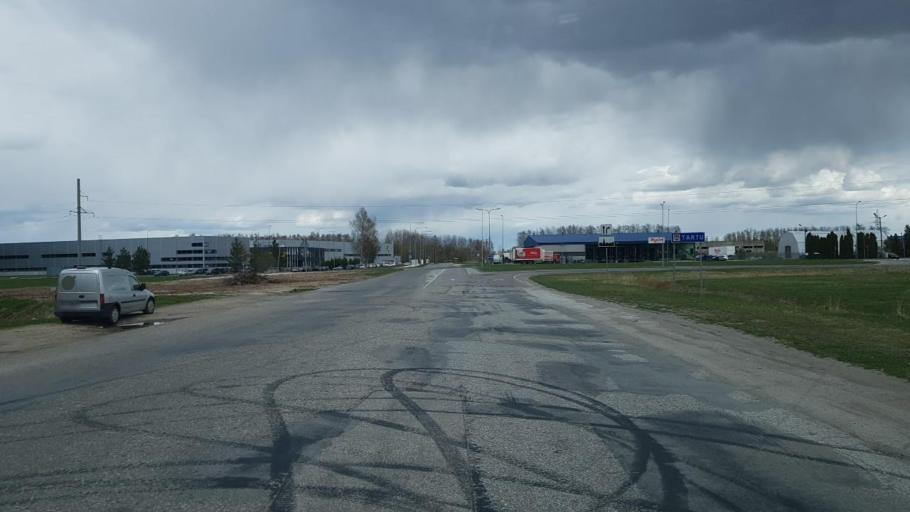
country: EE
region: Tartu
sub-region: Tartu linn
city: Tartu
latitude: 58.3894
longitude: 26.6757
